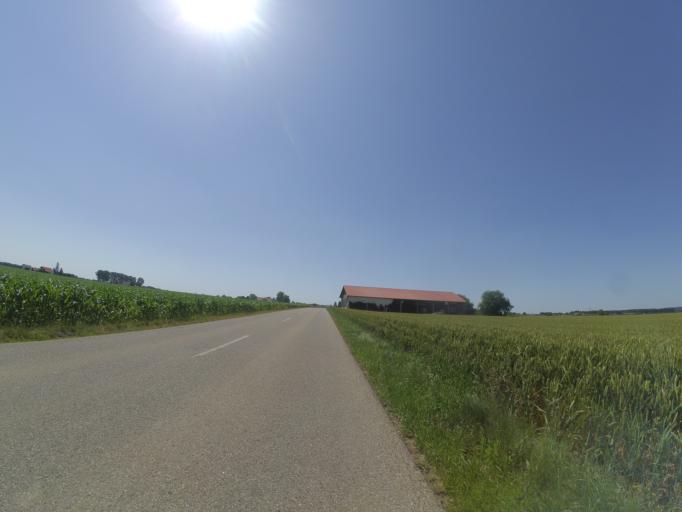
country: DE
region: Bavaria
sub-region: Swabia
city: Hawangen
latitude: 47.9704
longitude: 10.2443
